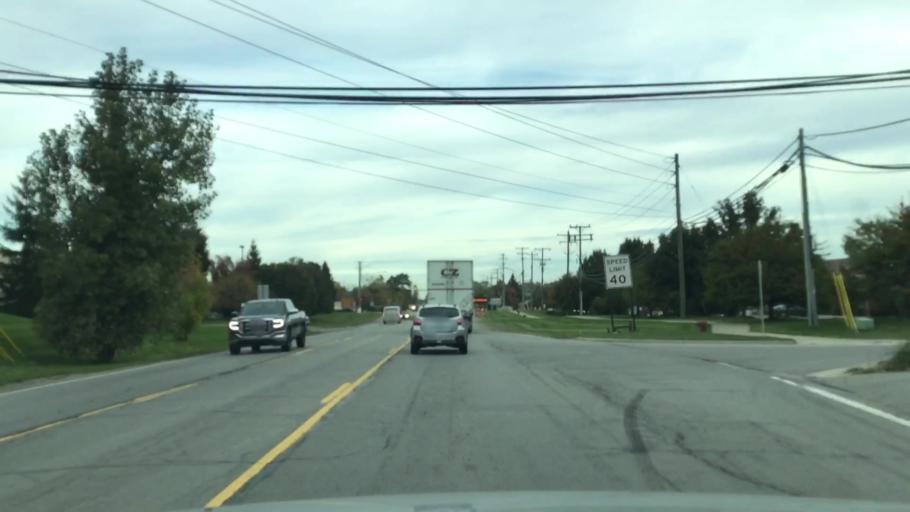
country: US
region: Michigan
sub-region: Oakland County
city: Wixom
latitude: 42.5068
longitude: -83.5164
